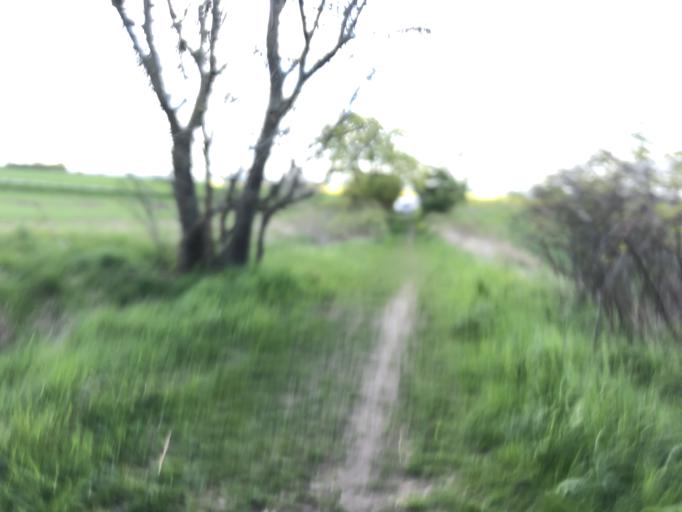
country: SE
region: Skane
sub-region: Staffanstorps Kommun
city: Staffanstorp
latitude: 55.6924
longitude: 13.2872
